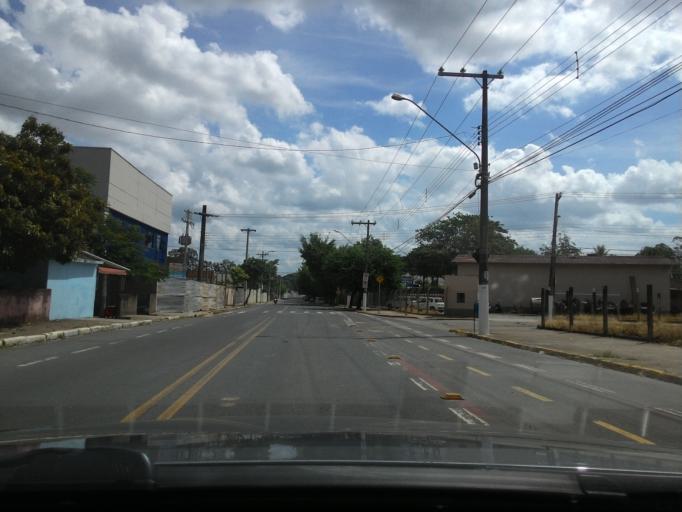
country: BR
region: Sao Paulo
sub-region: Registro
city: Registro
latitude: -24.5029
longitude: -47.8554
